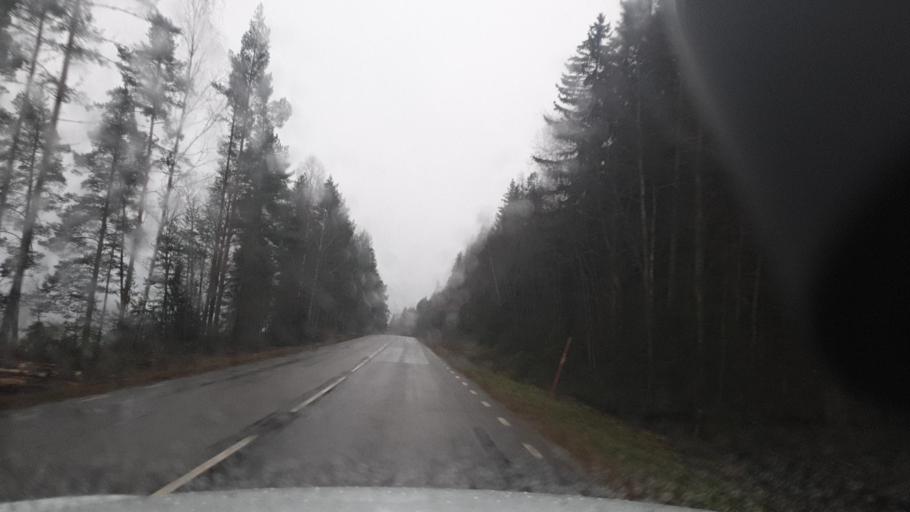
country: SE
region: Vaermland
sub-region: Arvika Kommun
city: Arvika
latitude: 59.7169
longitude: 12.6279
